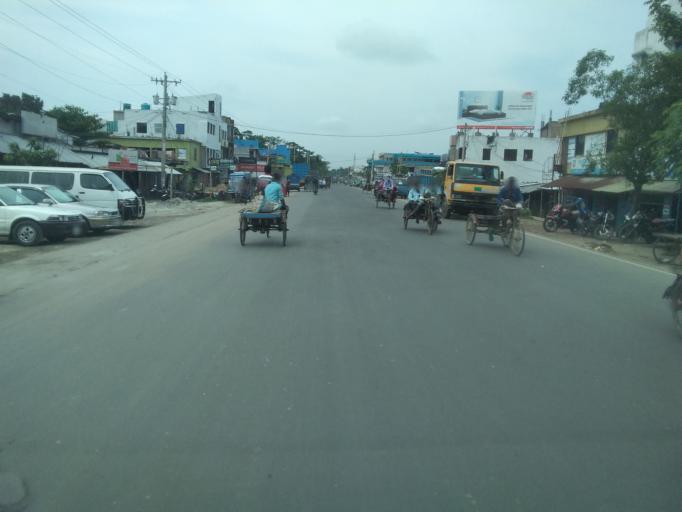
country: BD
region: Khulna
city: Kesabpur
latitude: 22.8397
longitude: 89.2947
